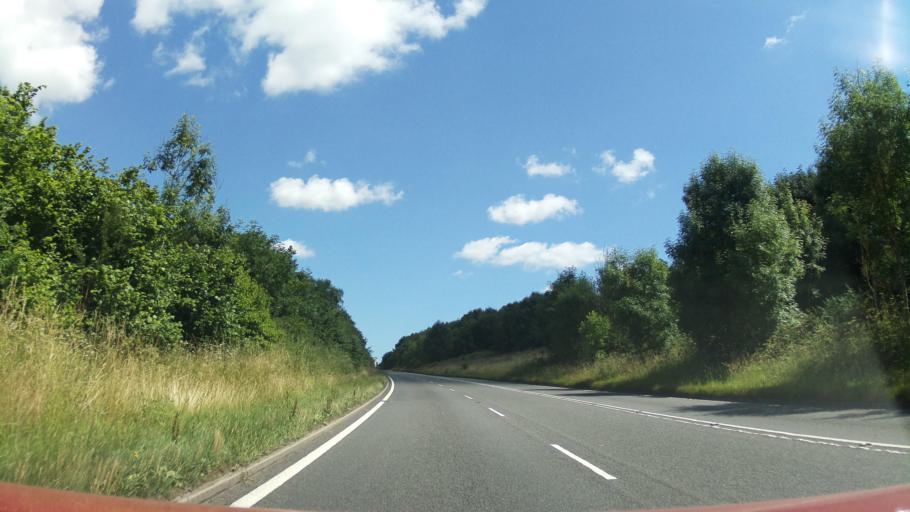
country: GB
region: England
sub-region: Derbyshire
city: Ashbourne
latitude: 53.0037
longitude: -1.7264
